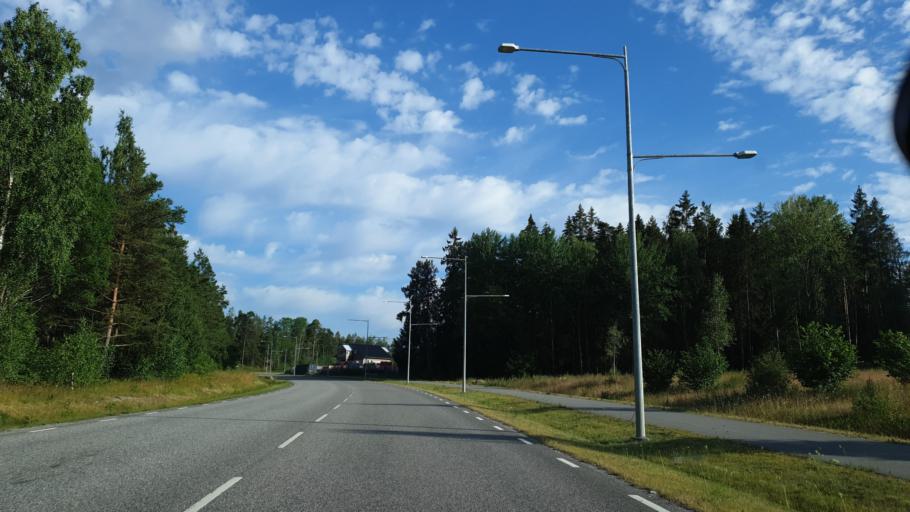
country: SE
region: Stockholm
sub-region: Sodertalje Kommun
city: Soedertaelje
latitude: 59.2183
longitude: 17.6510
